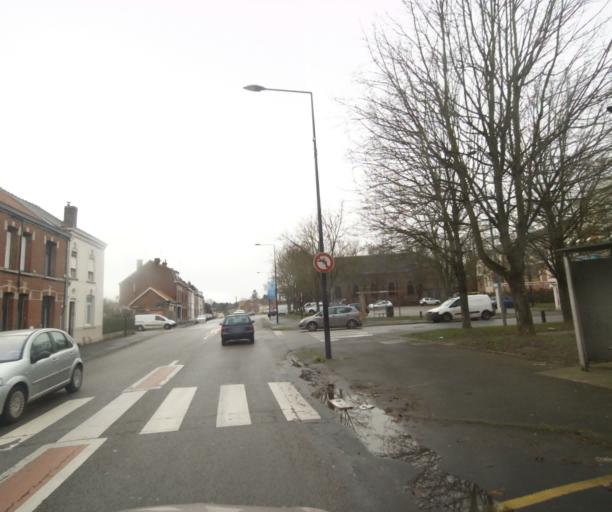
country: FR
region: Nord-Pas-de-Calais
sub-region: Departement du Nord
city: Valenciennes
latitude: 50.3429
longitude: 3.5258
